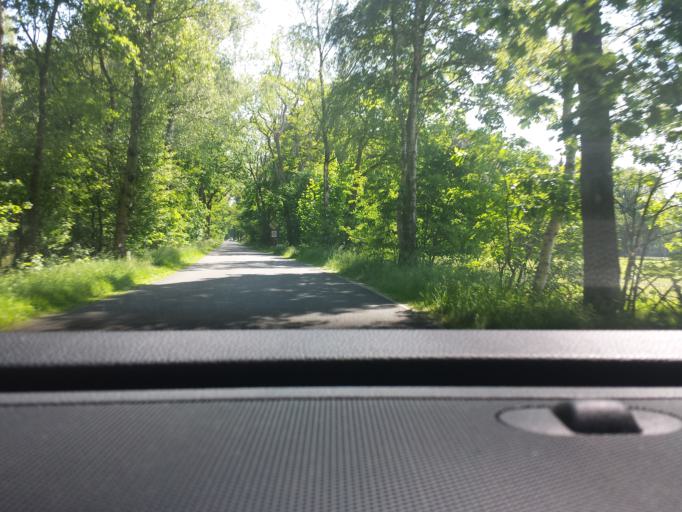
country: NL
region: Gelderland
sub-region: Gemeente Lochem
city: Almen
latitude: 52.1332
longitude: 6.3138
